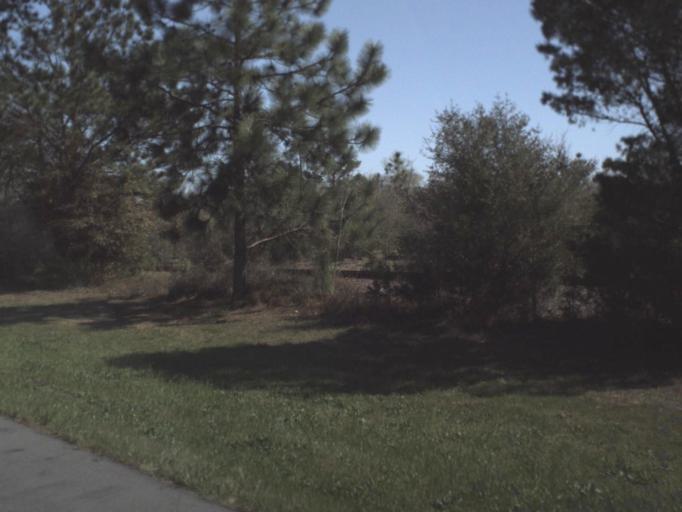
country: US
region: Florida
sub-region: Walton County
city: DeFuniak Springs
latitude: 30.7423
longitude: -86.1947
